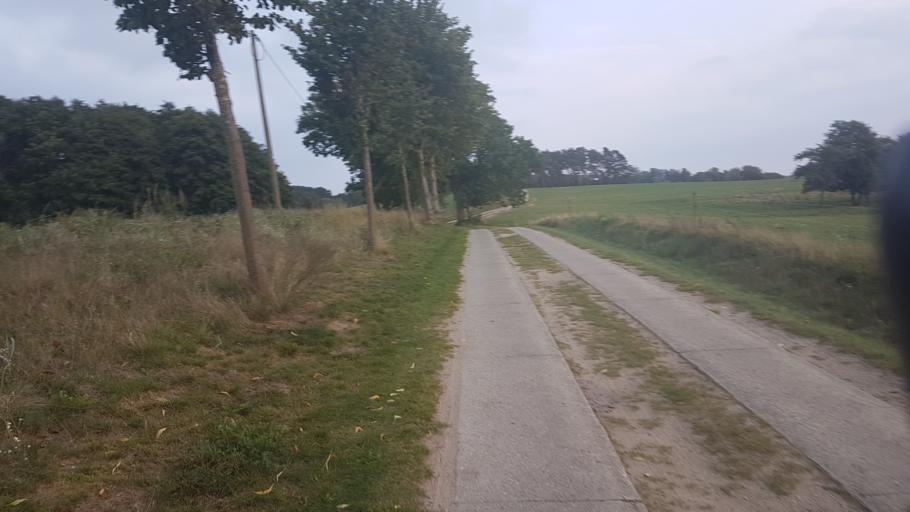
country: DE
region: Mecklenburg-Vorpommern
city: Putbus
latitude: 54.3519
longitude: 13.5280
